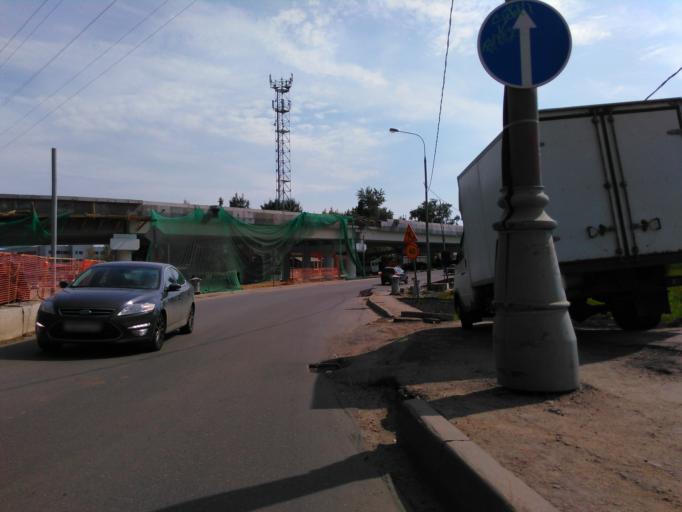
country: RU
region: Moskovskaya
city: Bol'shaya Setun'
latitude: 55.7100
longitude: 37.4053
